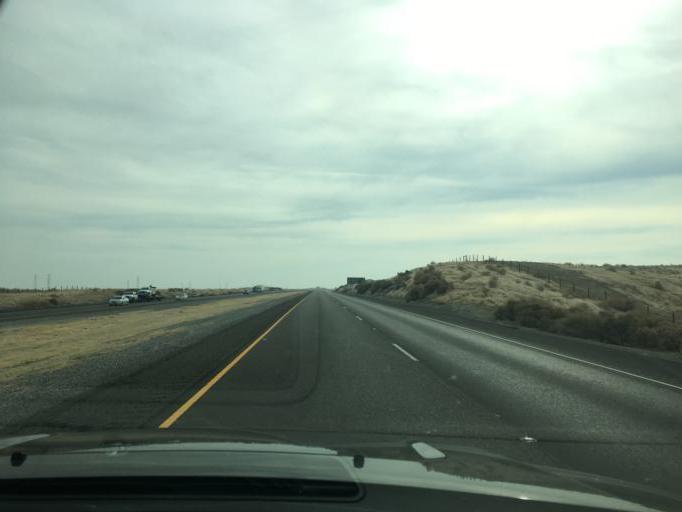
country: US
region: California
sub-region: Fresno County
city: Mendota
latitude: 36.5236
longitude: -120.4786
